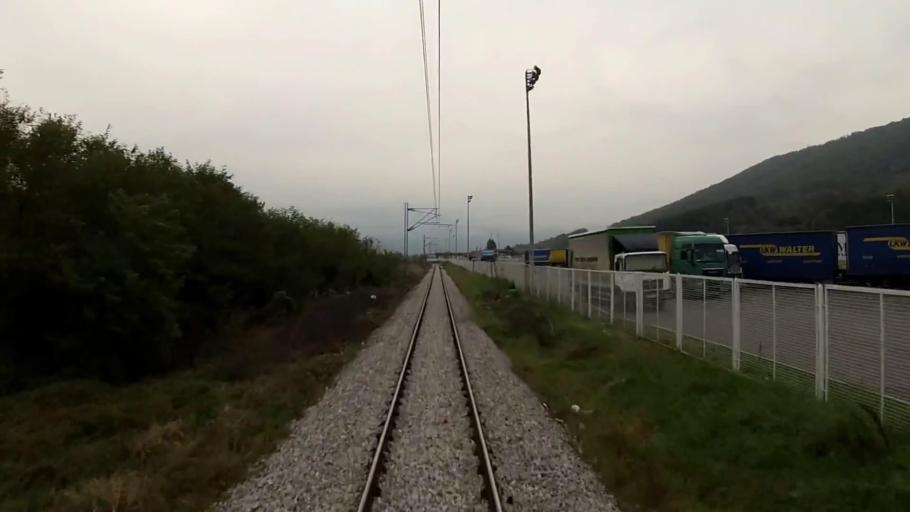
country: RS
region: Central Serbia
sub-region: Pirotski Okrug
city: Dimitrovgrad
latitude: 43.0015
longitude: 22.8245
